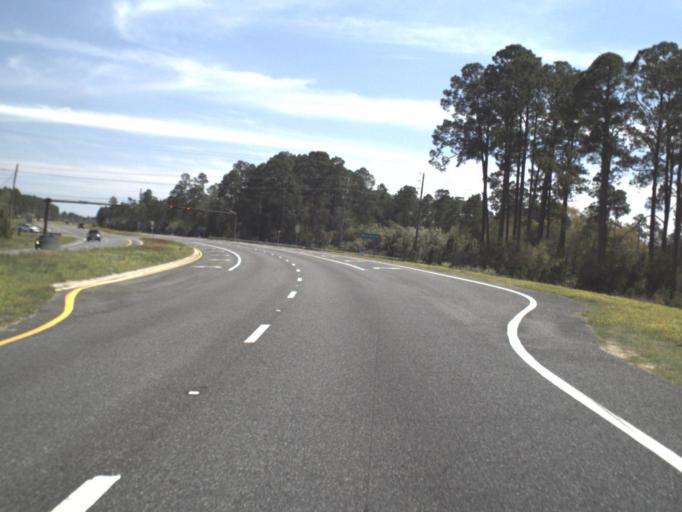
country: US
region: Florida
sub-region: Bay County
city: Lynn Haven
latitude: 30.3239
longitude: -85.6606
